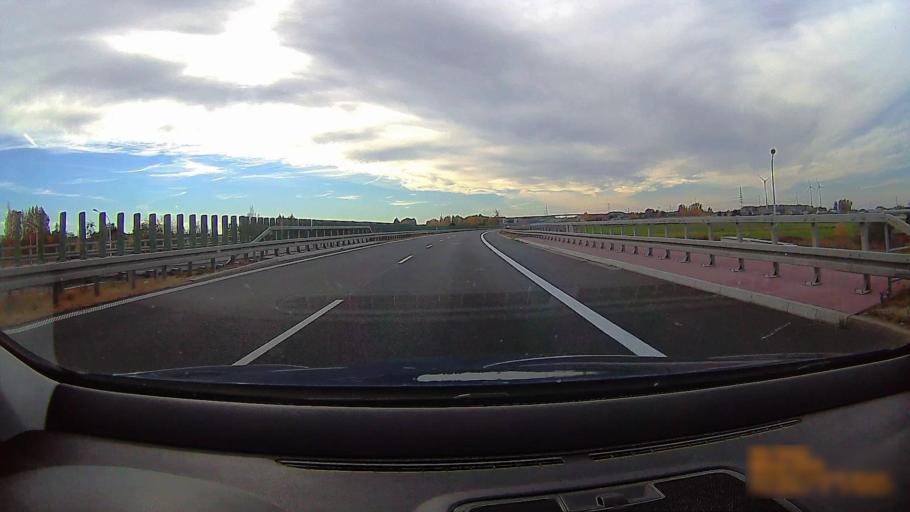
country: PL
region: Greater Poland Voivodeship
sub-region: Powiat ostrowski
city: Ostrow Wielkopolski
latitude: 51.6400
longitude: 17.8756
